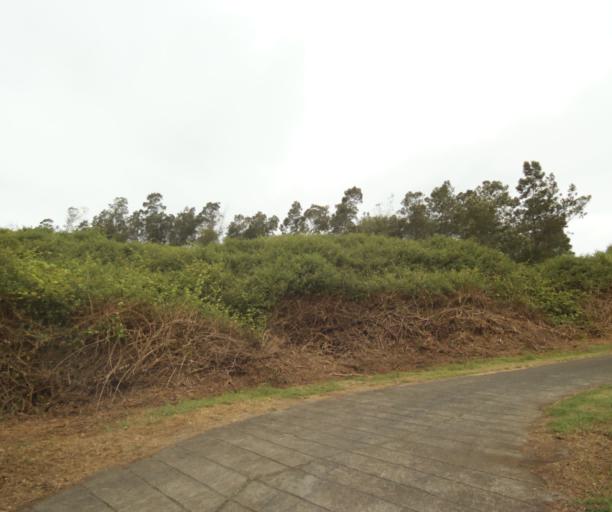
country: RE
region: Reunion
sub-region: Reunion
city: Saint-Paul
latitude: -21.0123
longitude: 55.3486
